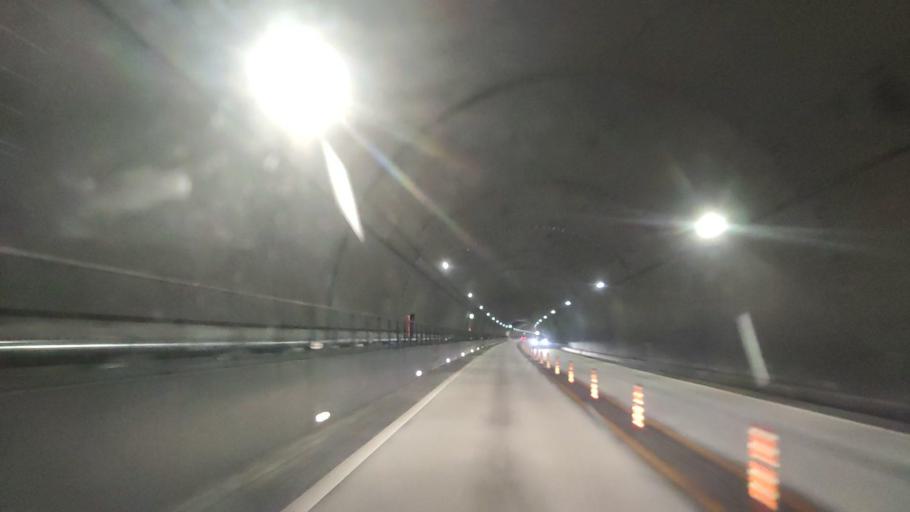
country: JP
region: Ehime
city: Hojo
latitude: 34.0811
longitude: 132.9768
